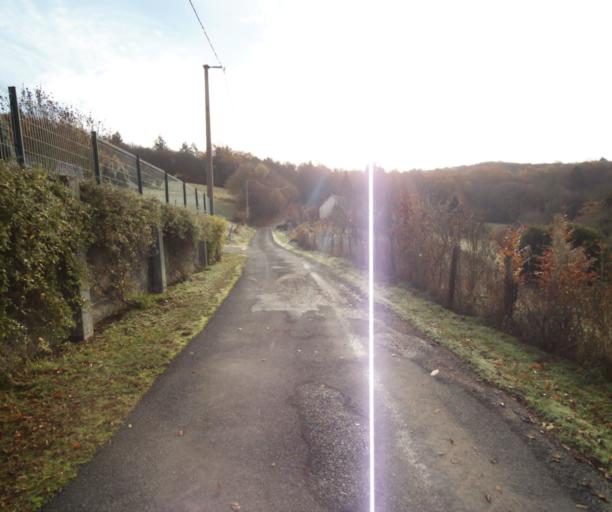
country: FR
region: Limousin
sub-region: Departement de la Correze
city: Chameyrat
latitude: 45.2227
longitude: 1.7263
